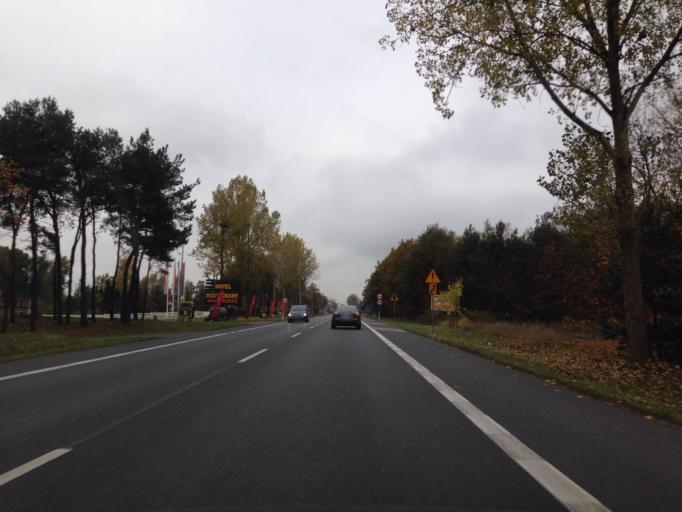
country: PL
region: Kujawsko-Pomorskie
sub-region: Powiat bydgoski
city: Osielsko
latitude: 53.2089
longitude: 18.1049
